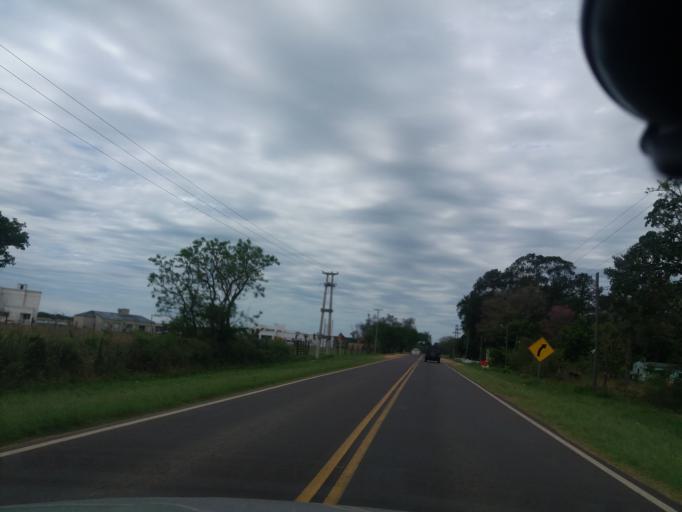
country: AR
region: Corrientes
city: Corrientes
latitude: -27.4561
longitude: -58.7165
